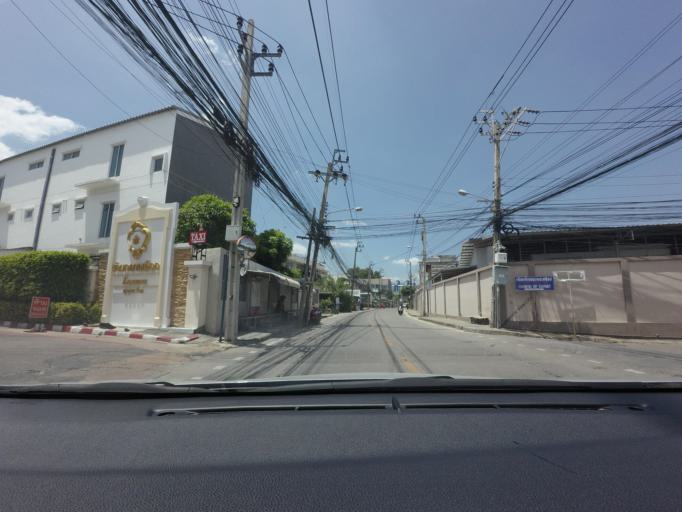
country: TH
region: Bangkok
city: Suan Luang
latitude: 13.7030
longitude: 100.6375
